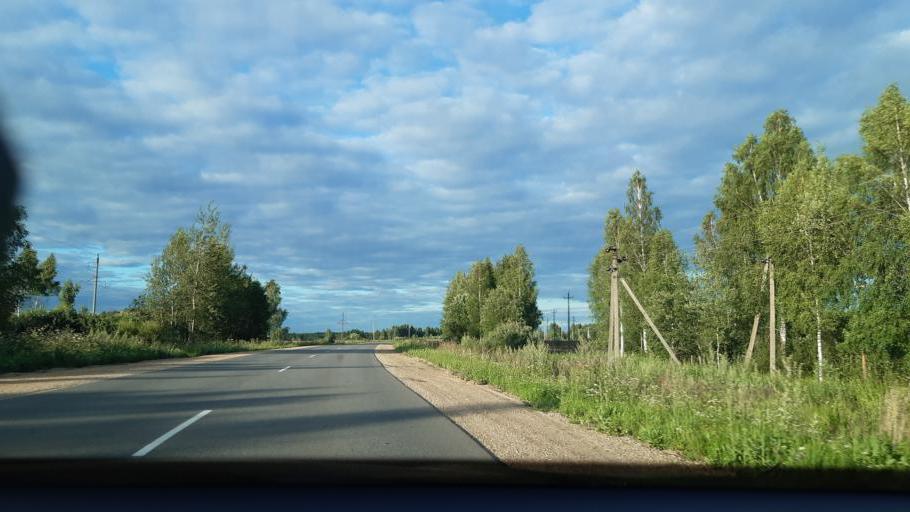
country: RU
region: Smolensk
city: Yel'nya
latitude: 54.5908
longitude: 33.1524
